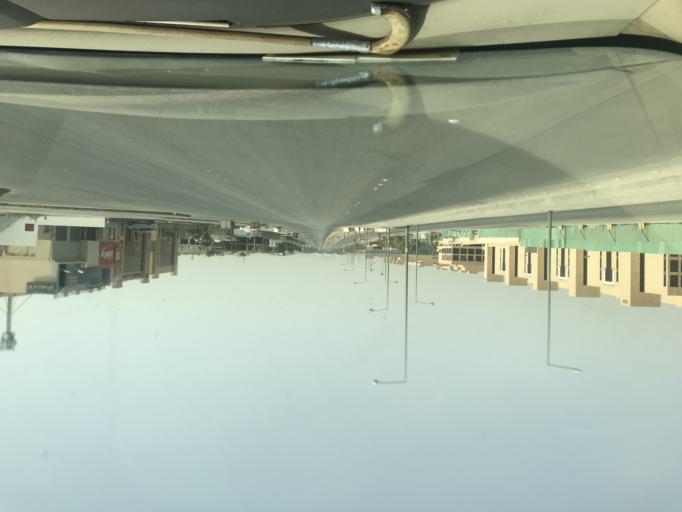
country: SA
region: Ar Riyad
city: Riyadh
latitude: 24.8158
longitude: 46.6887
